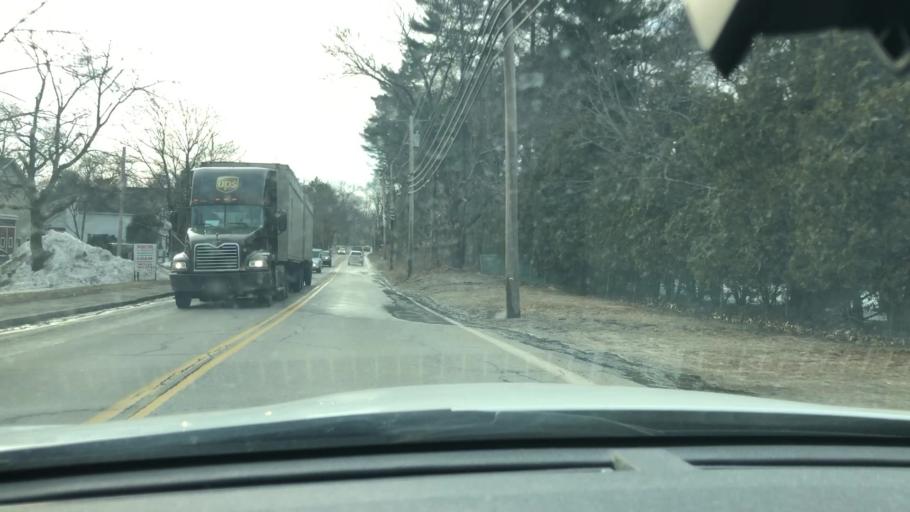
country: US
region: Massachusetts
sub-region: Middlesex County
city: Chelmsford
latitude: 42.5979
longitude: -71.3327
